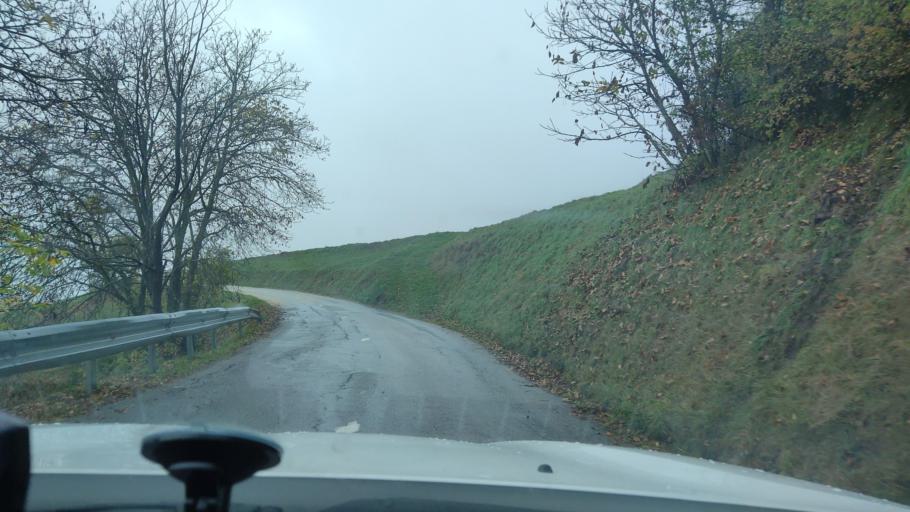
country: FR
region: Rhone-Alpes
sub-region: Departement de la Savoie
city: Les Allues
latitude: 45.4631
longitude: 6.5730
